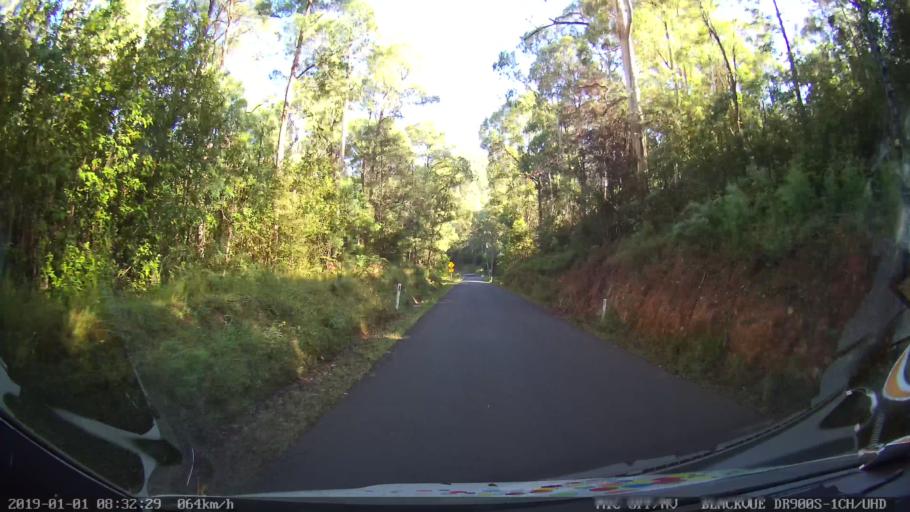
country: AU
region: New South Wales
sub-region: Snowy River
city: Jindabyne
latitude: -36.3615
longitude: 148.2061
